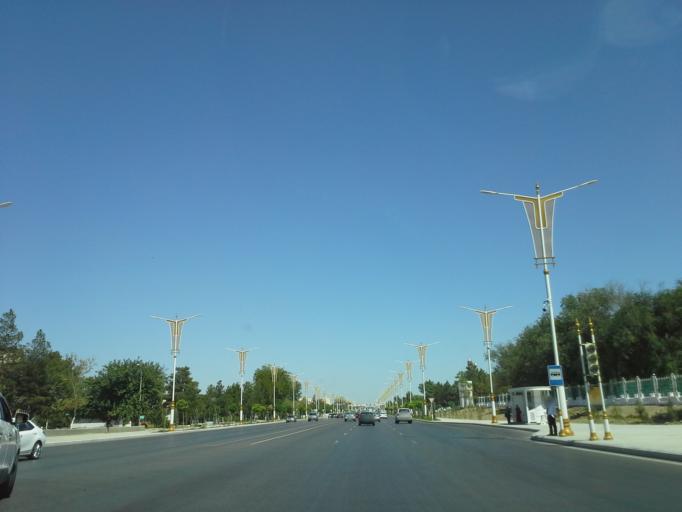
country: TM
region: Ahal
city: Ashgabat
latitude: 37.9101
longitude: 58.4119
